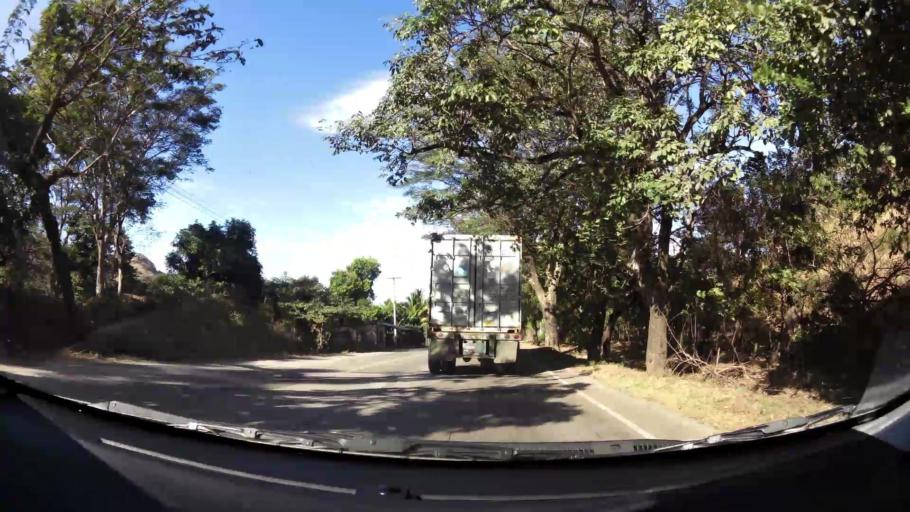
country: SV
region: Santa Ana
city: Texistepeque
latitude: 14.0755
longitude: -89.5025
